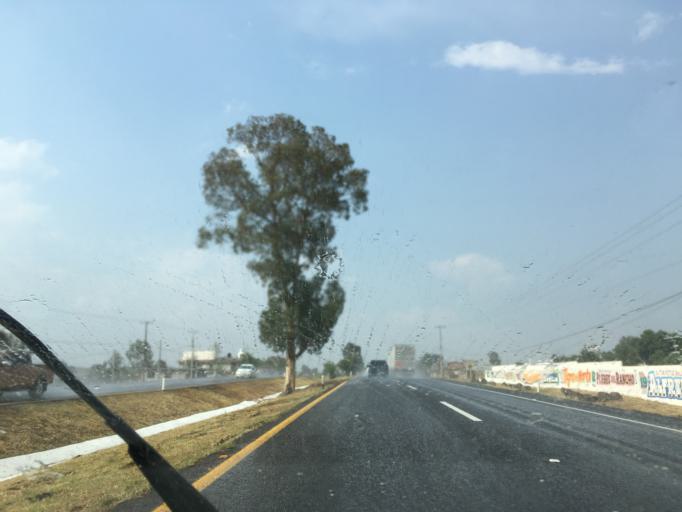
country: MX
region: Michoacan
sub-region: Morelia
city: La Mintzita (Piedra Dura)
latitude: 19.5910
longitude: -101.2993
